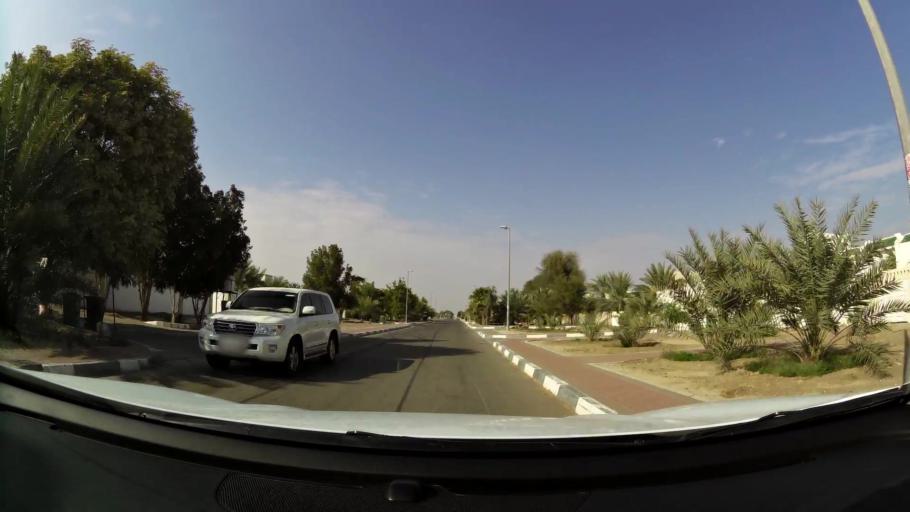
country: AE
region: Abu Dhabi
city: Al Ain
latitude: 24.0772
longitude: 55.8685
